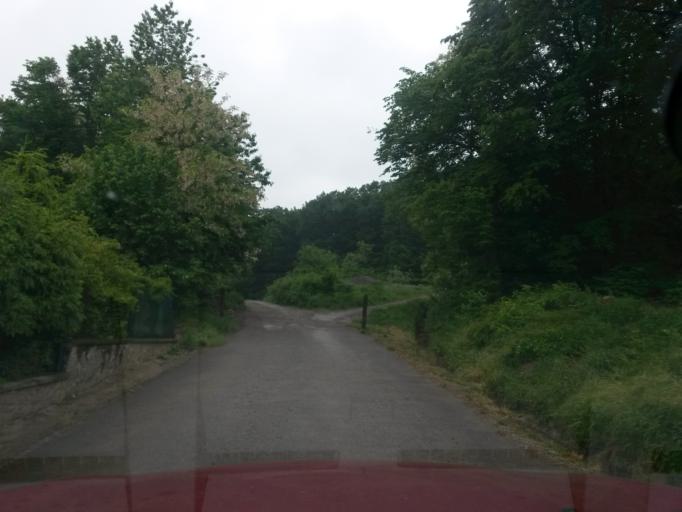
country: SK
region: Kosicky
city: Moldava nad Bodvou
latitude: 48.6969
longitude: 21.0682
